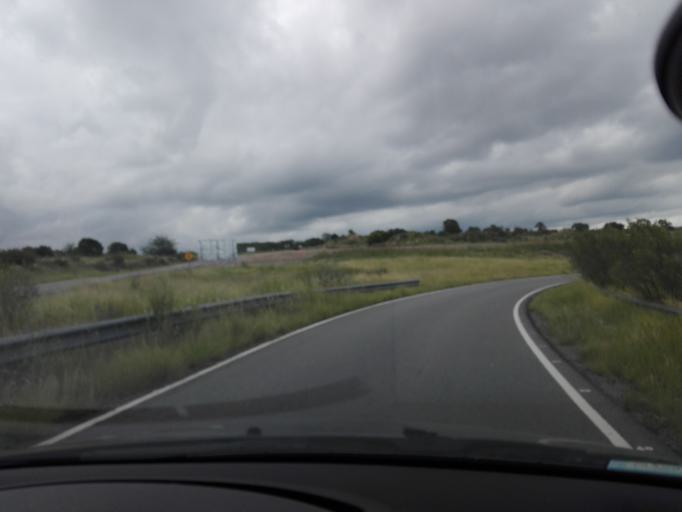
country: AR
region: Cordoba
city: Cuesta Blanca
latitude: -31.5694
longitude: -64.5886
